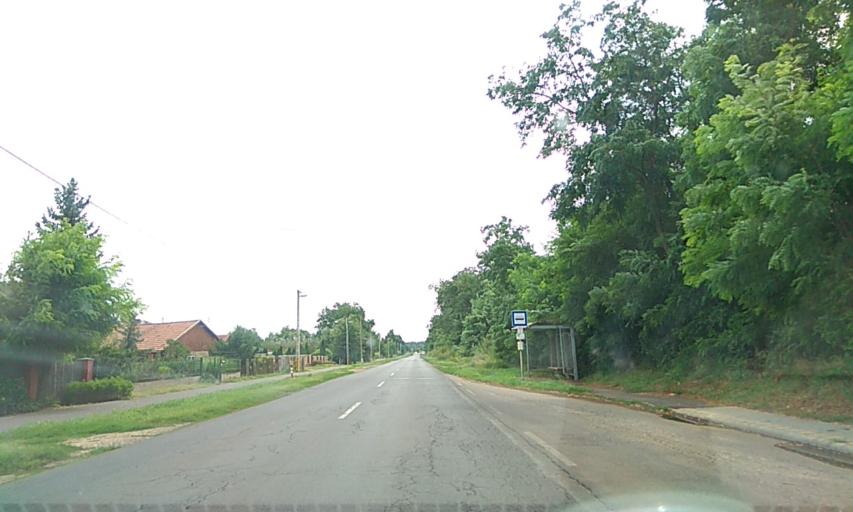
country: HU
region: Szabolcs-Szatmar-Bereg
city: Nyiregyhaza
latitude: 47.9968
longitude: 21.7023
